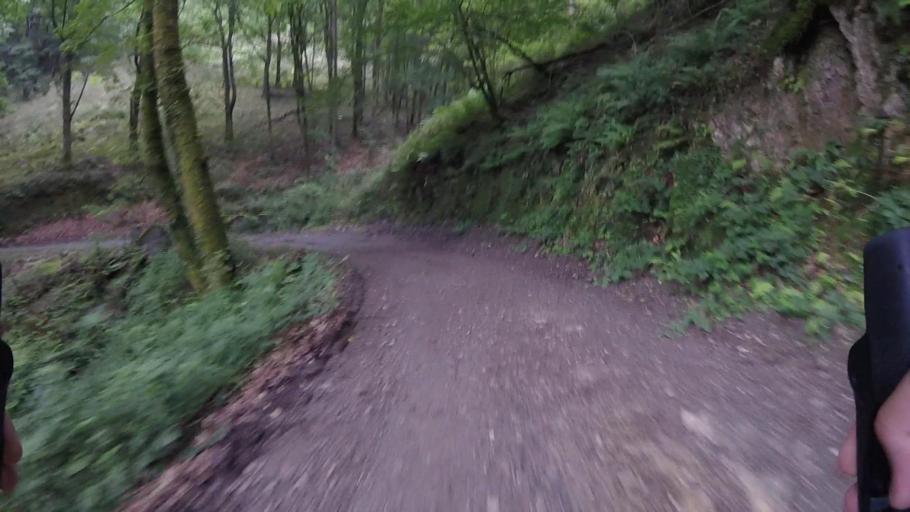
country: ES
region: Navarre
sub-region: Provincia de Navarra
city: Arano
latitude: 43.2536
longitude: -1.8546
